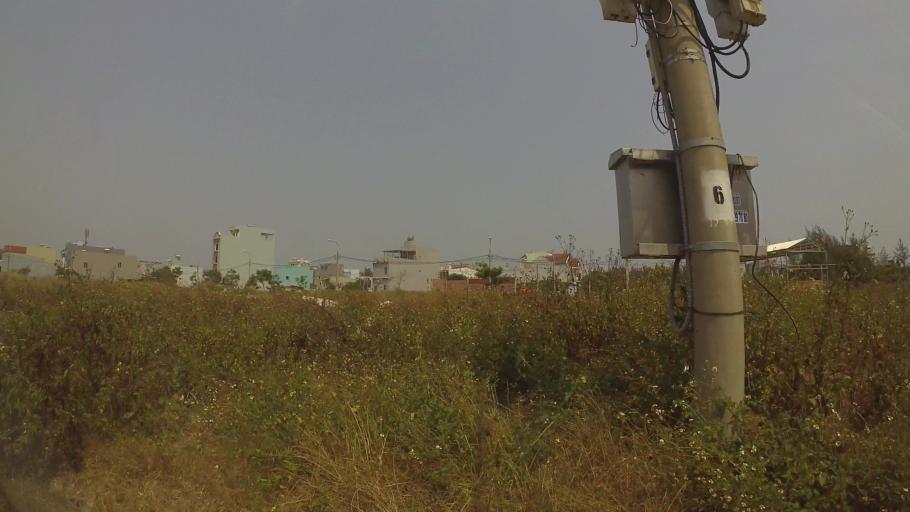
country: VN
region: Da Nang
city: Ngu Hanh Son
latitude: 15.9958
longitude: 108.2658
